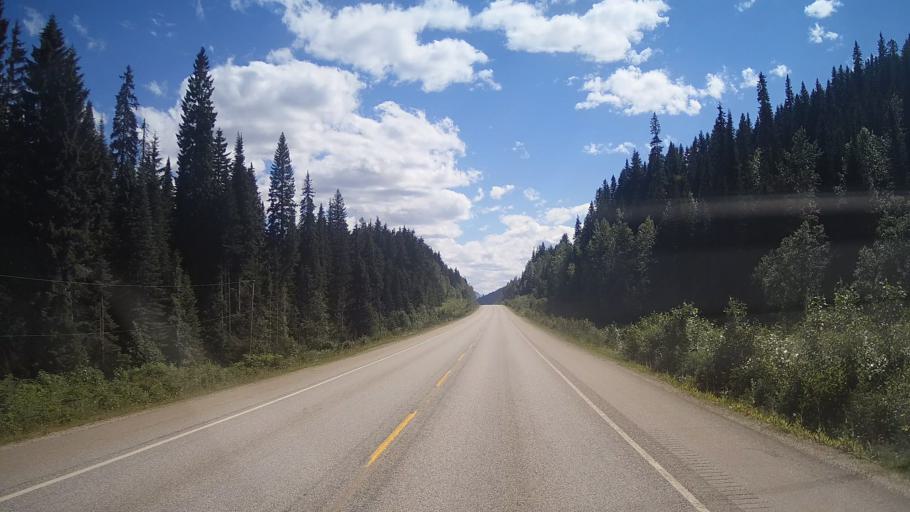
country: CA
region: Alberta
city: Jasper Park Lodge
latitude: 52.5585
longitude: -119.1103
